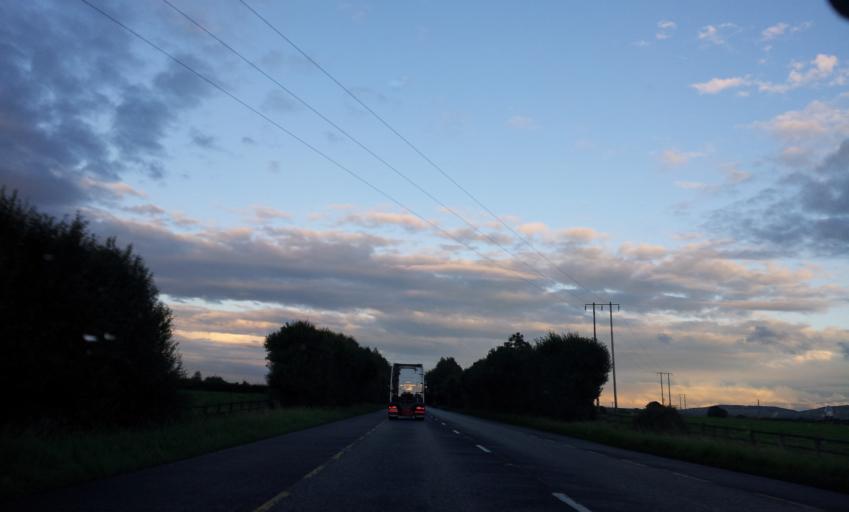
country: IE
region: Munster
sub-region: County Limerick
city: Rathkeale
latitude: 52.5293
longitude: -8.9021
